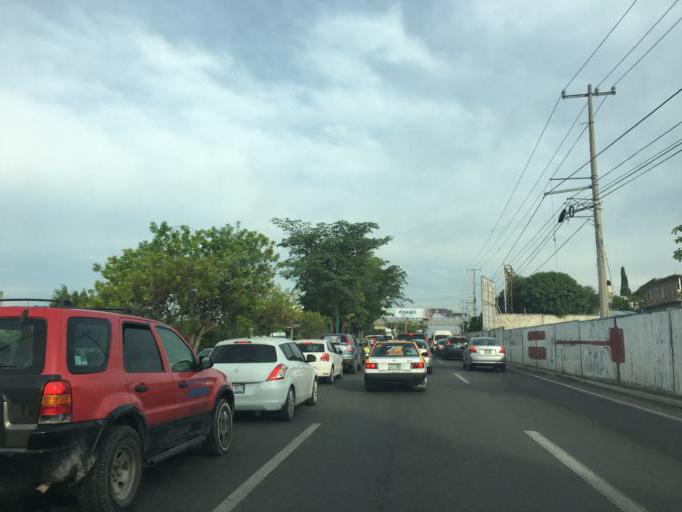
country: MX
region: Chiapas
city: Tuxtla Gutierrez
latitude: 16.7632
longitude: -93.1565
